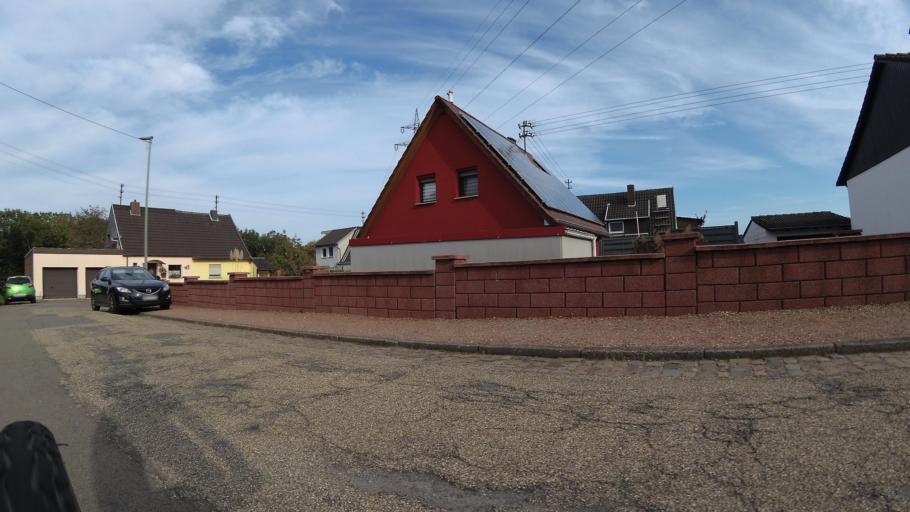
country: DE
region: Saarland
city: Friedrichsthal
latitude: 49.3336
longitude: 7.0870
